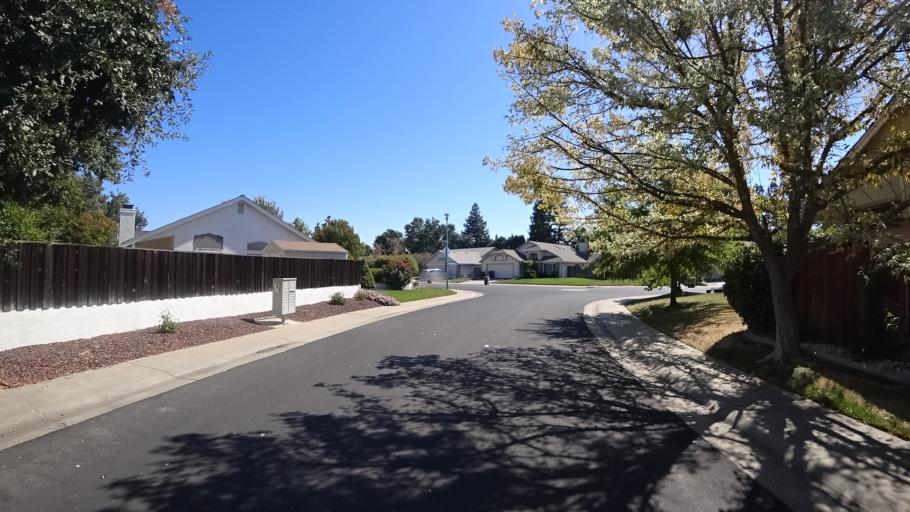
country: US
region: California
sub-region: Sacramento County
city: Laguna
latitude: 38.4370
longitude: -121.4321
